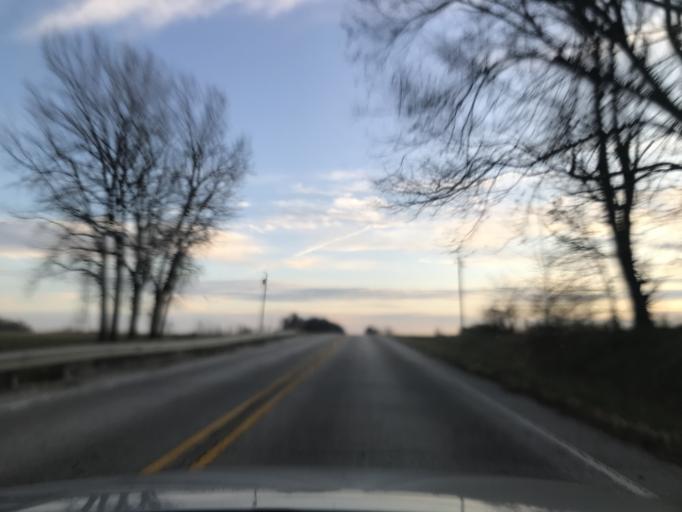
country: US
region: Illinois
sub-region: Henderson County
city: Oquawka
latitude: 40.9775
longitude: -90.8639
